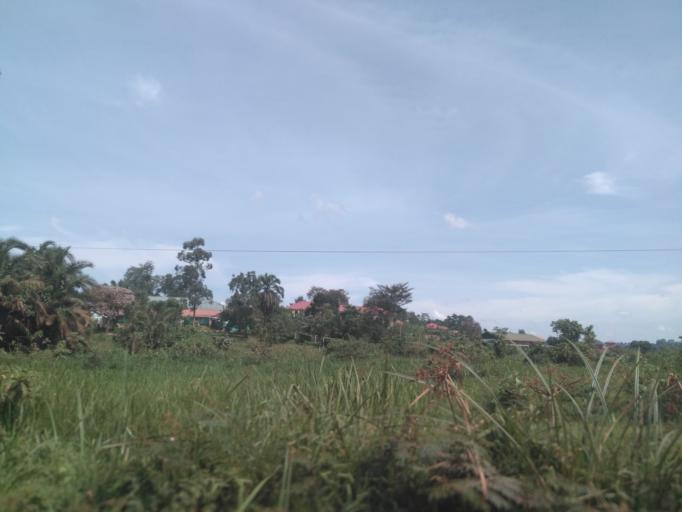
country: UG
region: Central Region
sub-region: Wakiso District
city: Kireka
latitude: 0.4410
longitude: 32.5931
